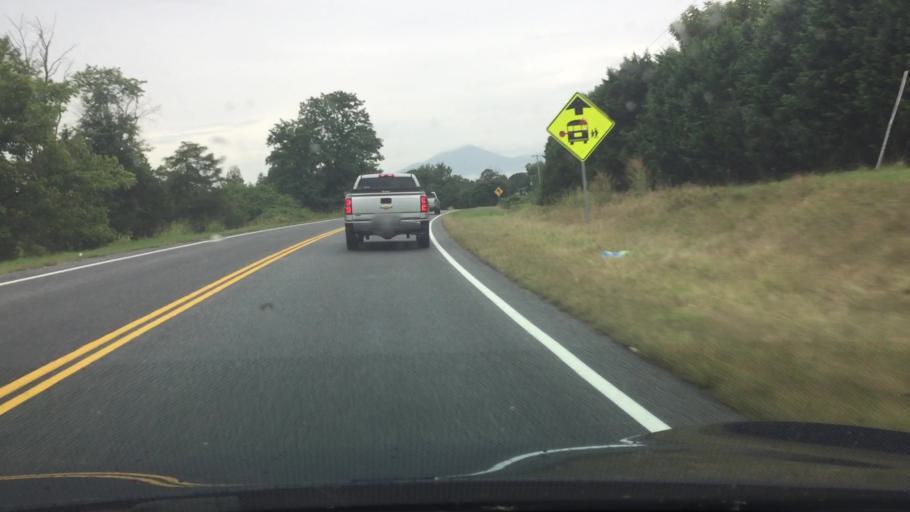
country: US
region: Virginia
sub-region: Bedford County
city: Forest
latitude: 37.3663
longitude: -79.4051
